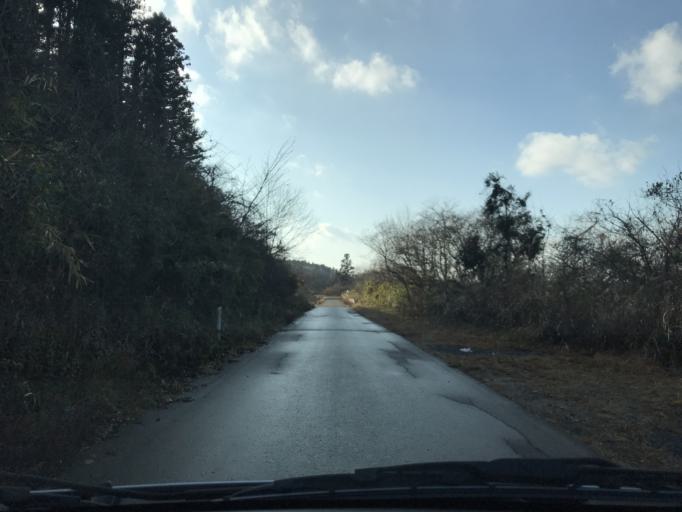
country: JP
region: Miyagi
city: Wakuya
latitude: 38.6883
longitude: 141.1124
